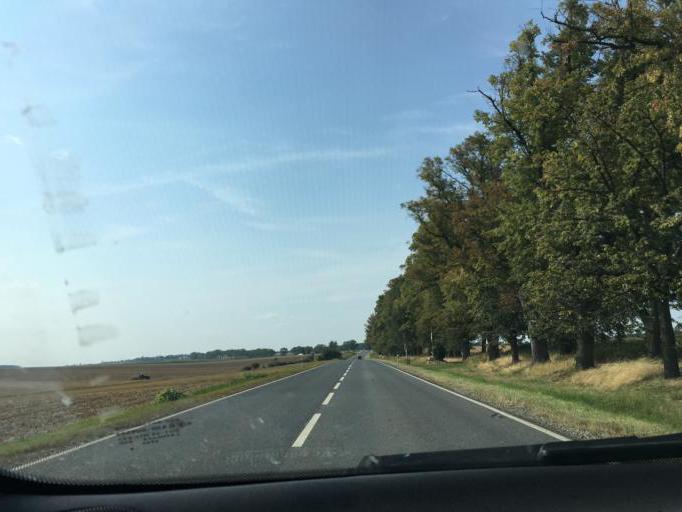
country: PL
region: Opole Voivodeship
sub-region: Powiat prudnicki
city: Laka Prudnicka
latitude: 50.4147
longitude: 17.4904
